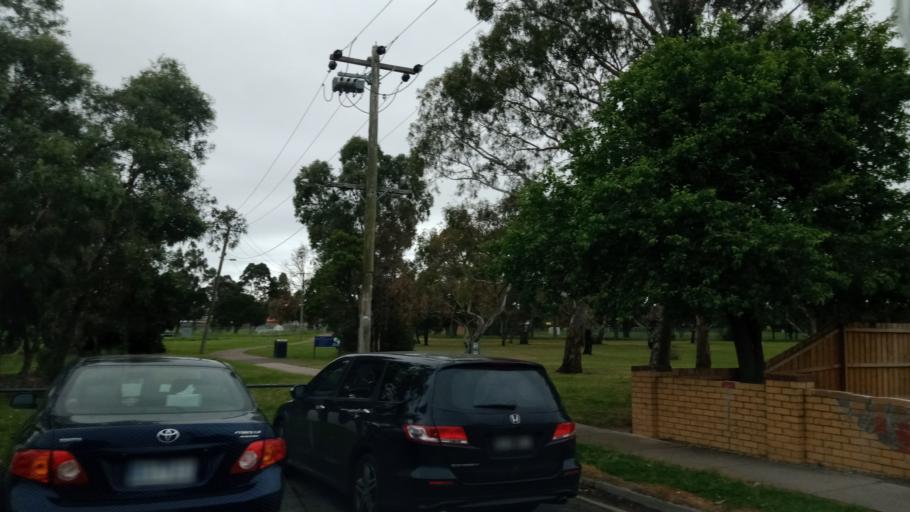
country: AU
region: Victoria
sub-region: Greater Dandenong
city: Springvale
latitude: -37.9472
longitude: 145.1592
